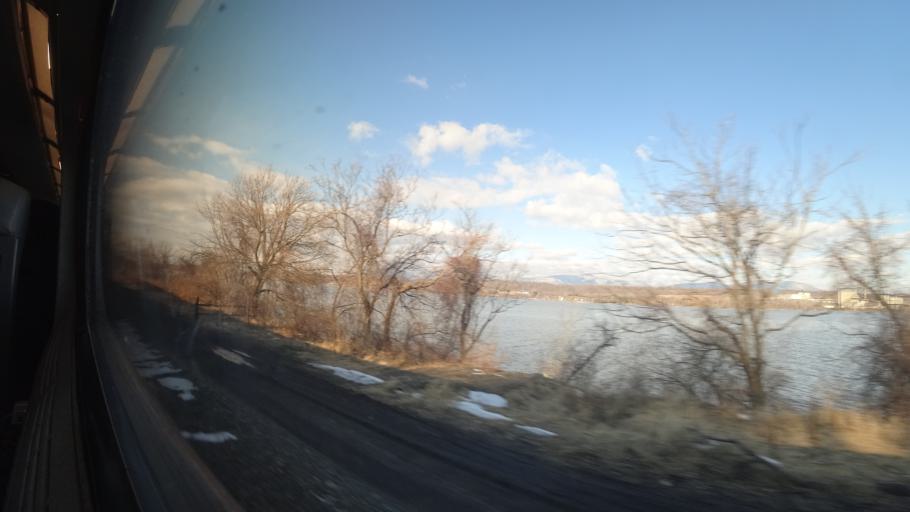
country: US
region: New York
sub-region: Dutchess County
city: Tivoli
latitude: 42.1303
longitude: -73.9008
